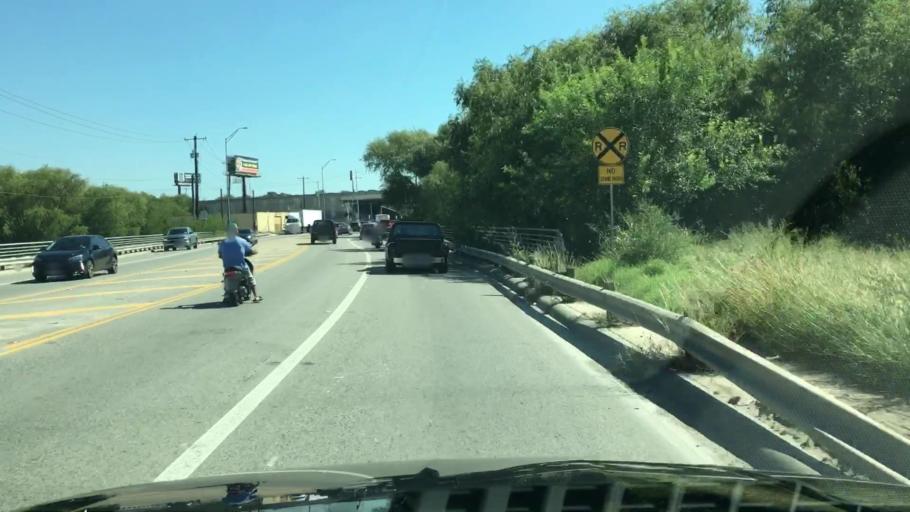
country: US
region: Texas
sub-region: Bexar County
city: Windcrest
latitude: 29.5344
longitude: -98.3922
